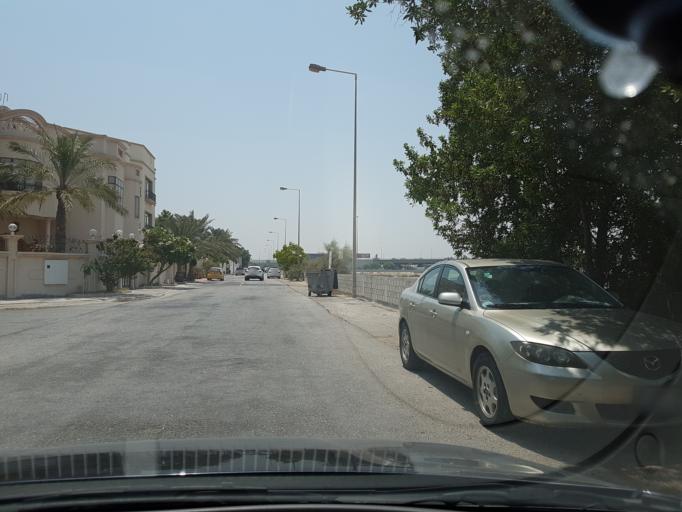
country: BH
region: Manama
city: Manama
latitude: 26.2080
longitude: 50.5699
